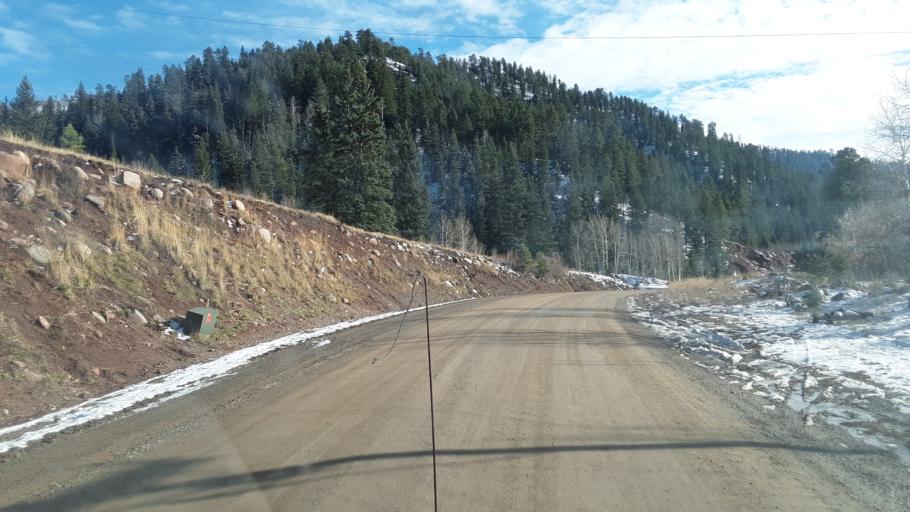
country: US
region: Colorado
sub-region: La Plata County
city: Bayfield
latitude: 37.3957
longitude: -107.6578
